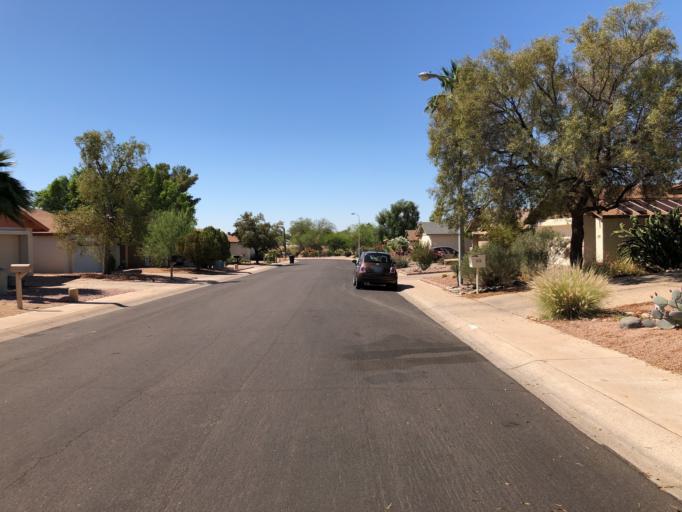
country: US
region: Arizona
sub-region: Maricopa County
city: Tempe
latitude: 33.4564
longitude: -111.8986
